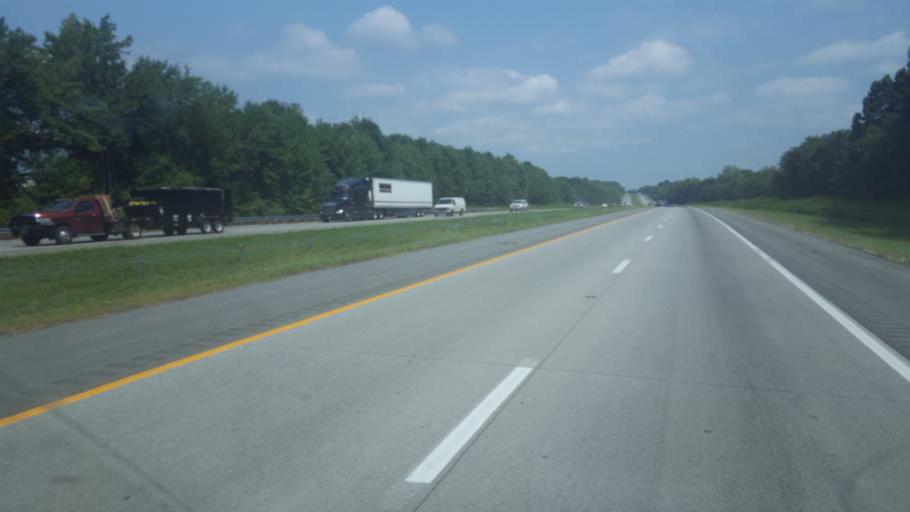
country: US
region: North Carolina
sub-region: Yadkin County
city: Jonesville
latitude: 36.1459
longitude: -80.8080
